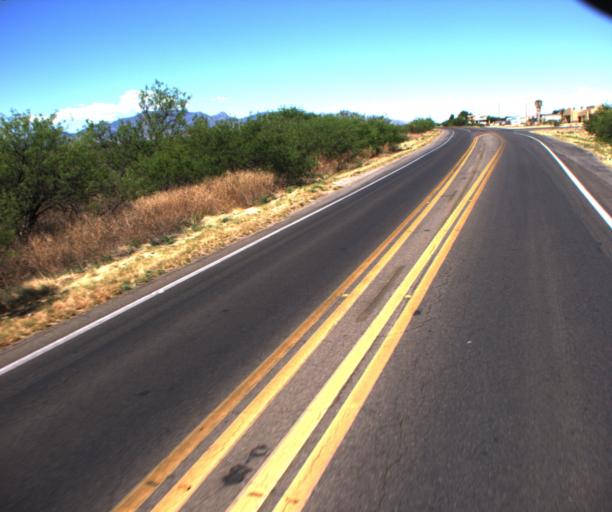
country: US
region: Arizona
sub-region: Cochise County
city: Sierra Vista
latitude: 31.5544
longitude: -110.2052
